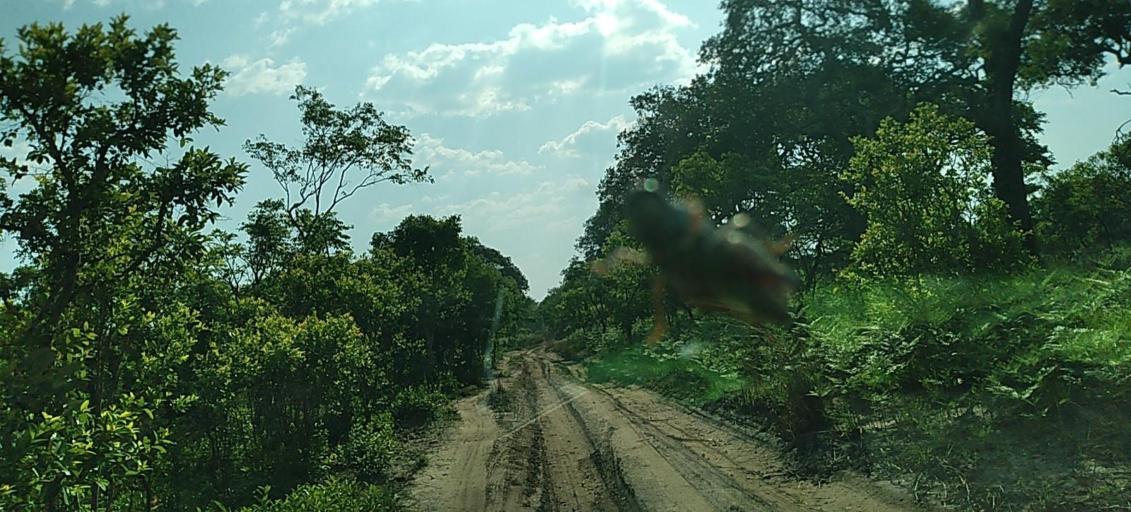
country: ZM
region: North-Western
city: Mwinilunga
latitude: -11.3086
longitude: 24.7852
